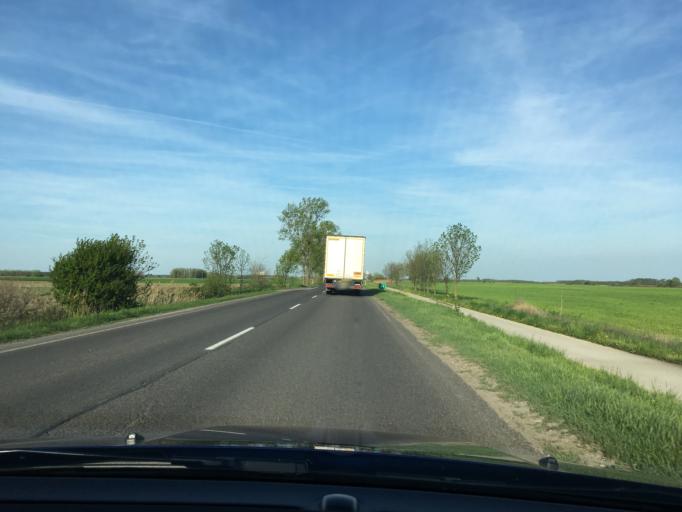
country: HU
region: Bekes
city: Korosladany
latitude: 46.9989
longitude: 21.1017
